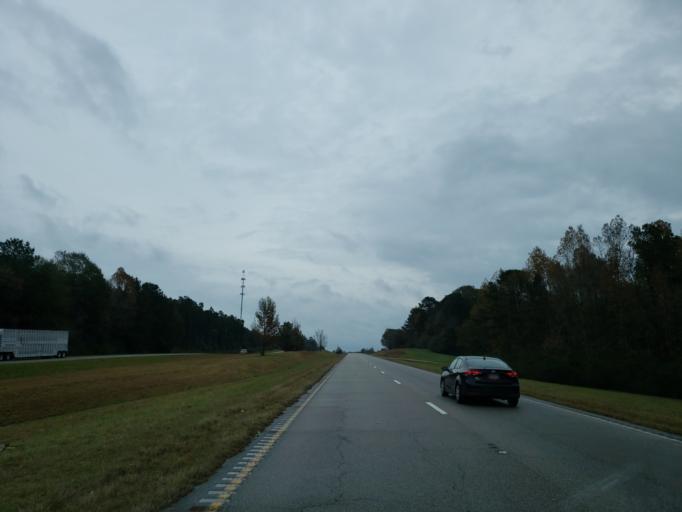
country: US
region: Mississippi
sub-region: Jones County
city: Sharon
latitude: 31.7049
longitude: -88.9267
